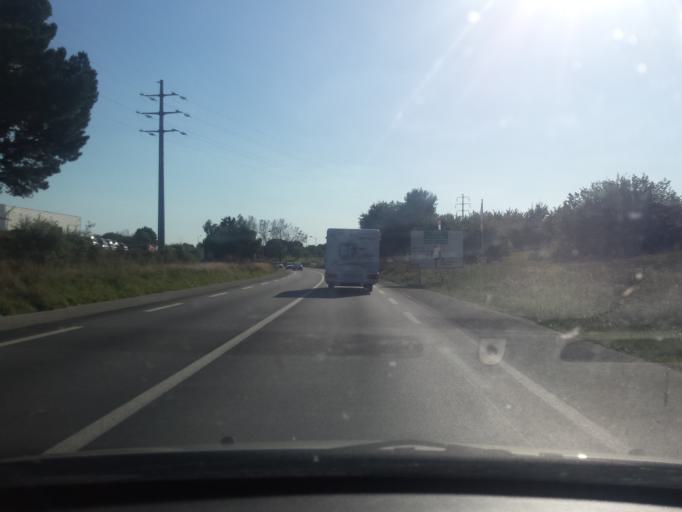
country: FR
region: Brittany
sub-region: Departement du Morbihan
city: Vannes
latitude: 47.6786
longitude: -2.7733
